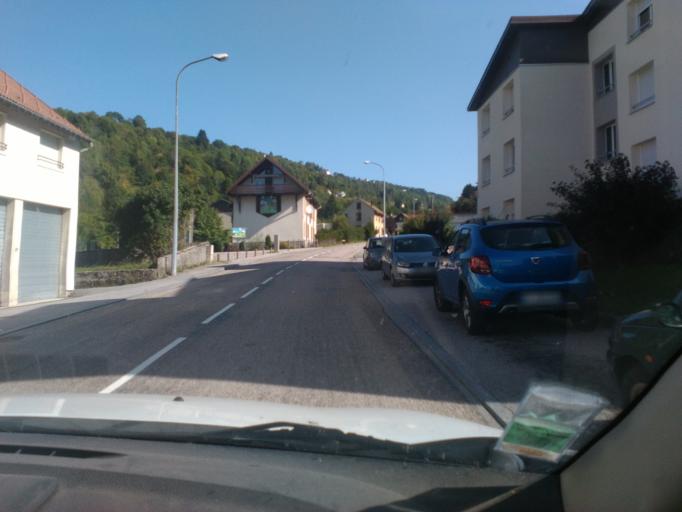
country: FR
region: Lorraine
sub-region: Departement des Vosges
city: La Bresse
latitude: 48.0157
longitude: 6.8935
